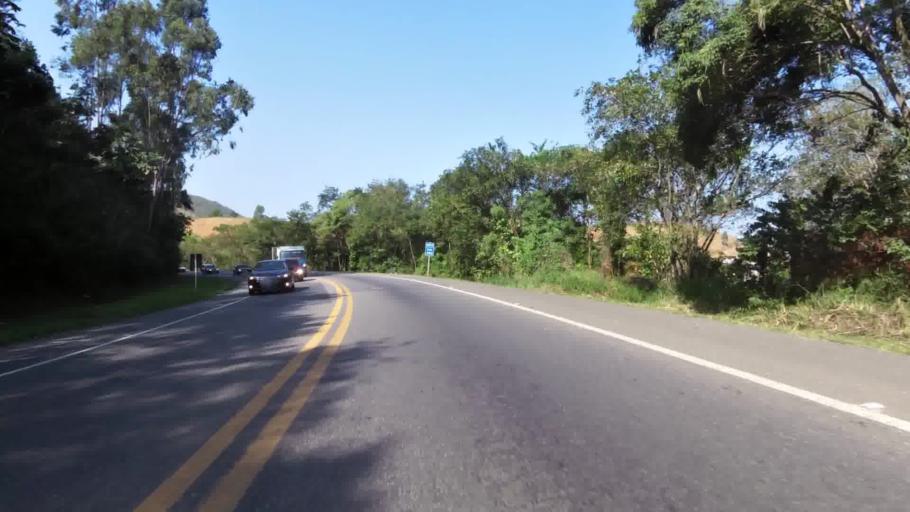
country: BR
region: Espirito Santo
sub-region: Rio Novo Do Sul
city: Rio Novo do Sul
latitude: -20.8674
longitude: -40.9048
